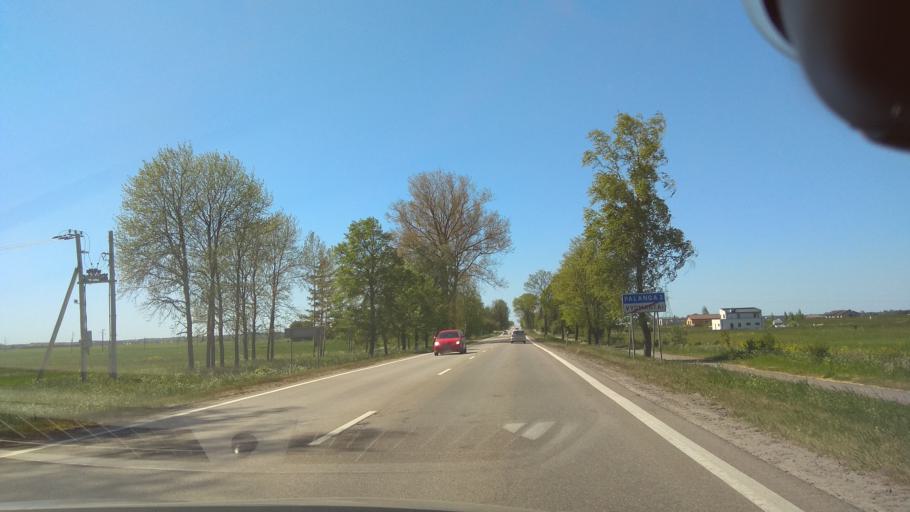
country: LT
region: Klaipedos apskritis
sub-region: Klaipeda
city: Palanga
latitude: 55.9022
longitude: 21.1291
